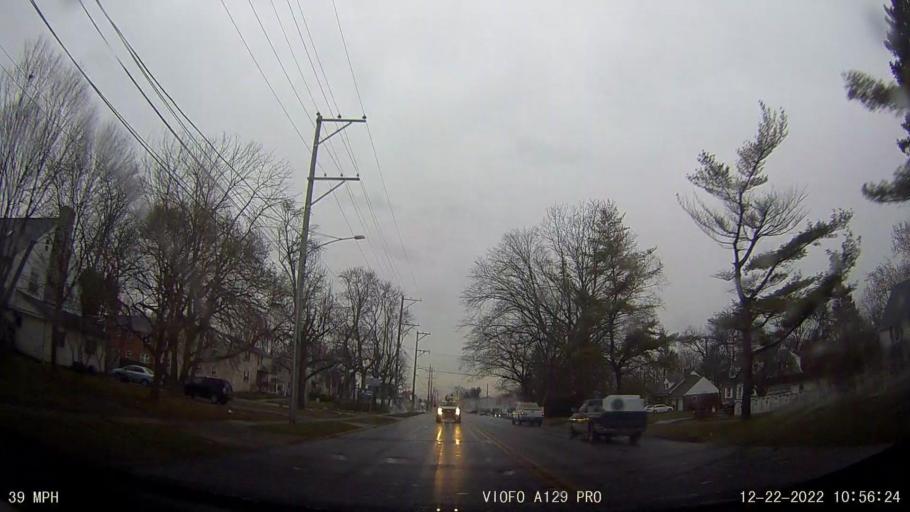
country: US
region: Pennsylvania
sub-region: Montgomery County
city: West Norriton
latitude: 40.1256
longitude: -75.3661
